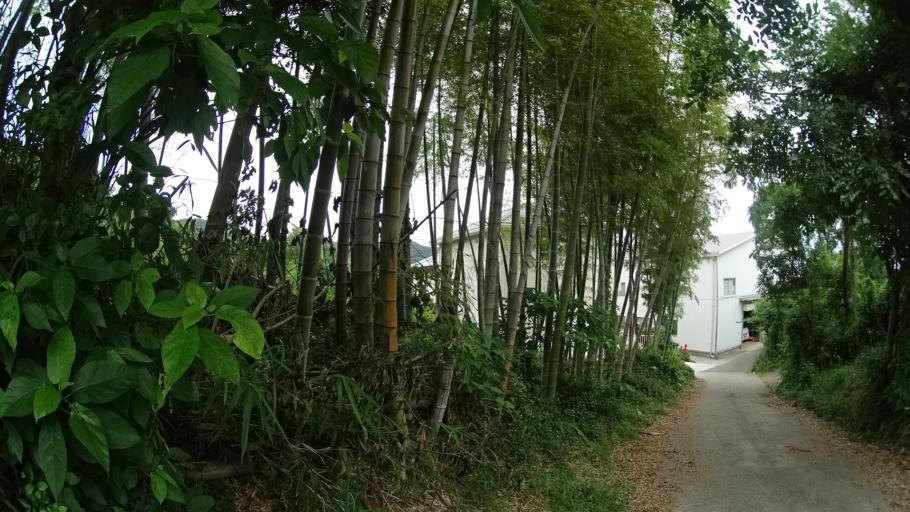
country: JP
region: Kanagawa
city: Yokosuka
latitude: 35.2123
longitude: 139.6565
